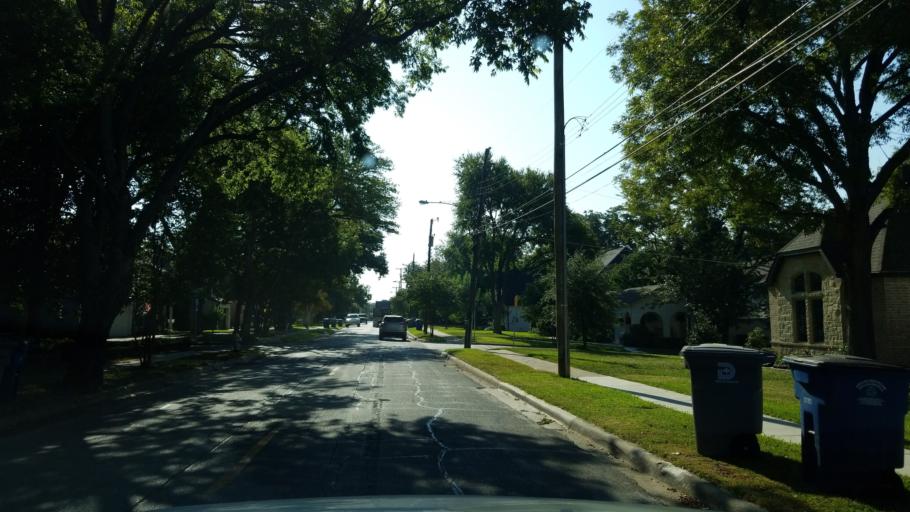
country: US
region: Texas
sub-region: Dallas County
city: Highland Park
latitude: 32.8094
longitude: -96.7345
